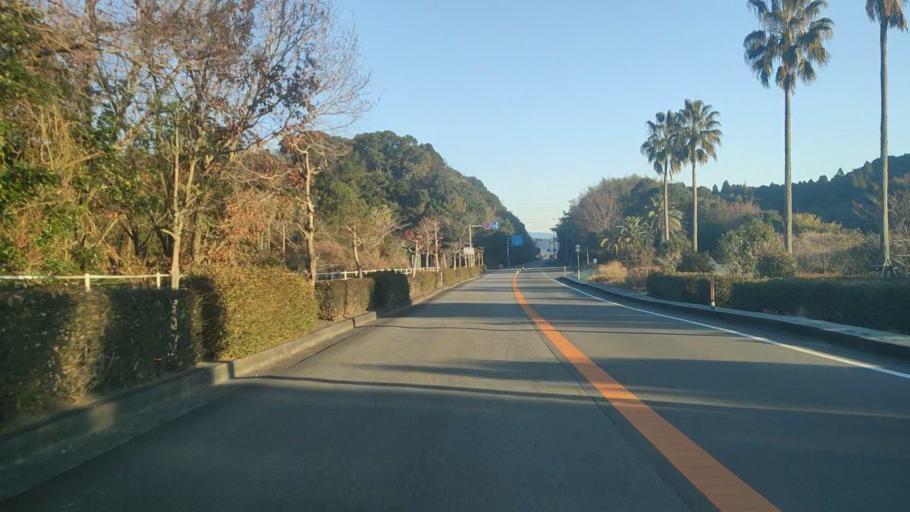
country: JP
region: Miyazaki
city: Tsuma
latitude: 32.0284
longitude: 131.4641
